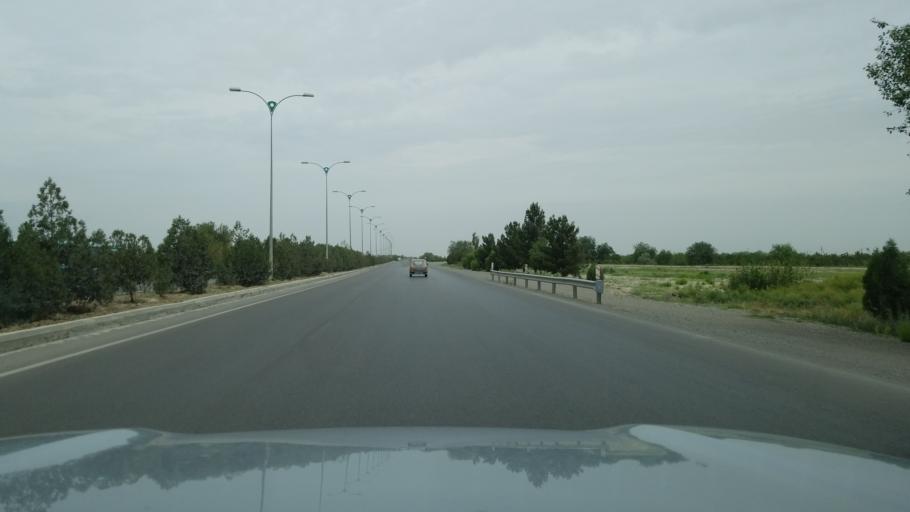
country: TM
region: Ahal
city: Abadan
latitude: 38.1087
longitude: 58.0631
